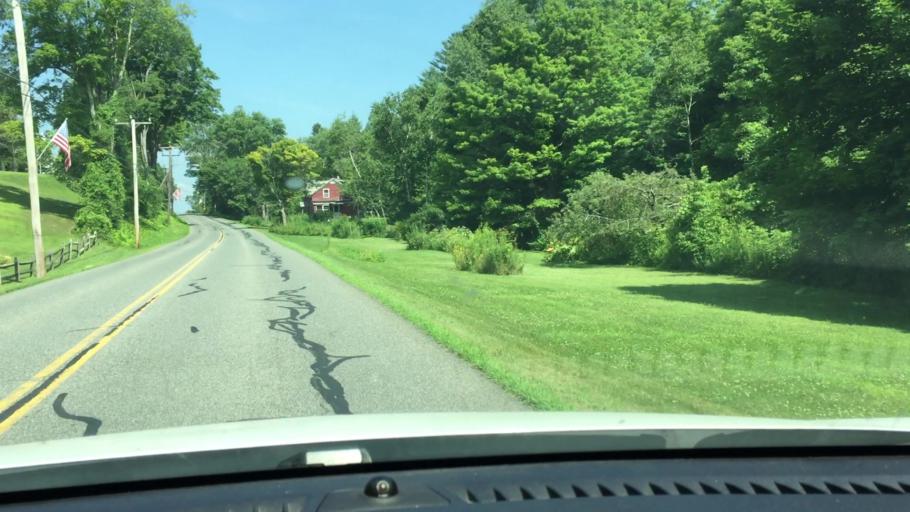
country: US
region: Massachusetts
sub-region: Berkshire County
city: Lee
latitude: 42.2425
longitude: -73.1995
